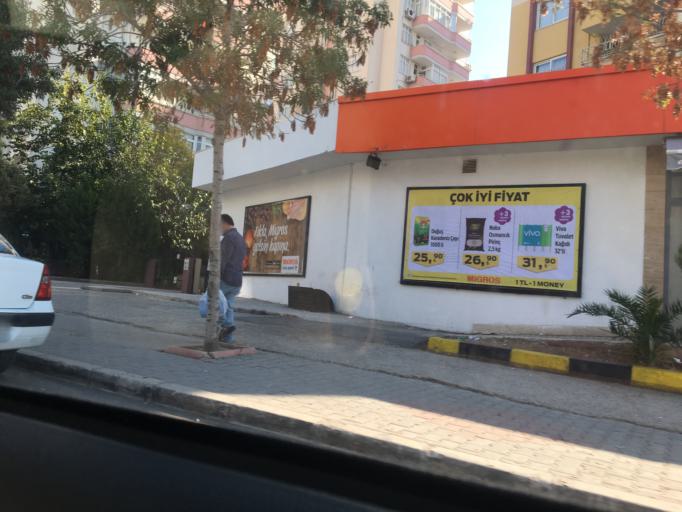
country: TR
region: Adana
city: Seyhan
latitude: 37.0359
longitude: 35.2814
